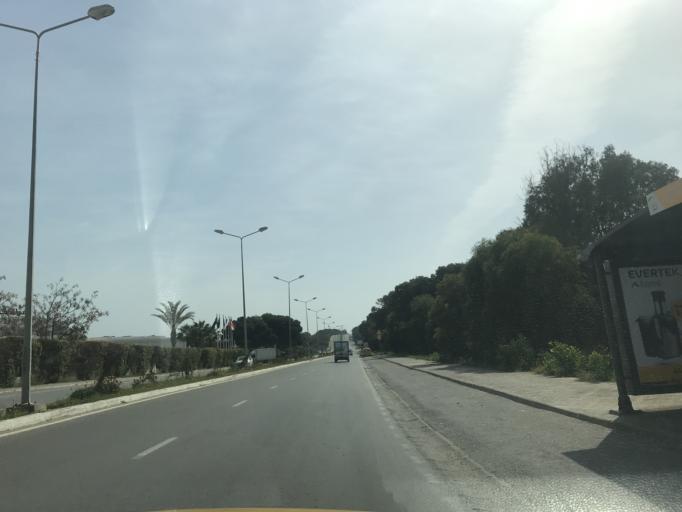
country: TN
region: Tunis
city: Al Marsa
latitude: 36.9208
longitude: 10.2865
